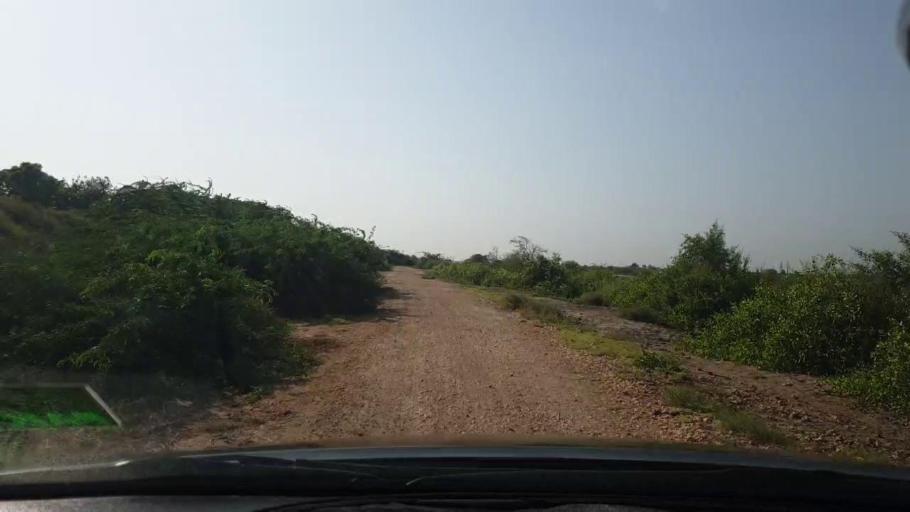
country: PK
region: Sindh
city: Tando Bago
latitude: 24.7141
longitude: 68.9779
